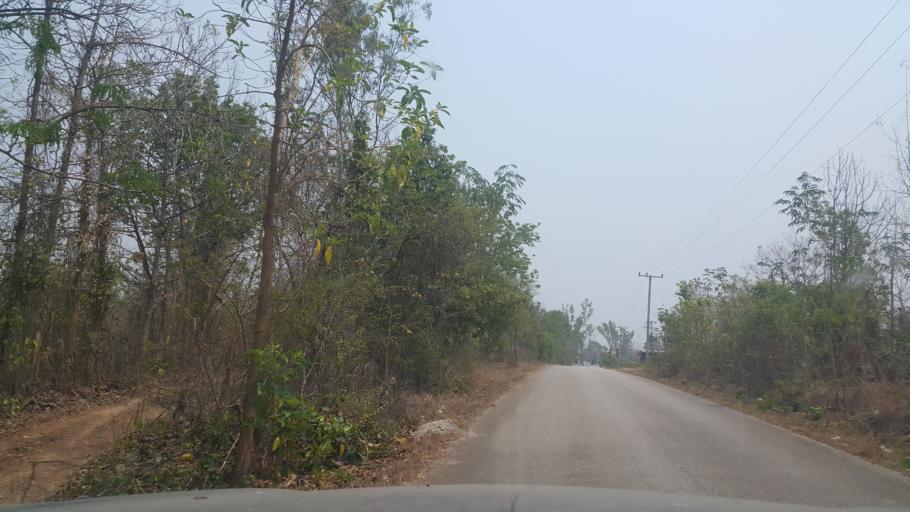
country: TH
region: Lampang
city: Sop Prap
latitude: 17.8968
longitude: 99.3169
